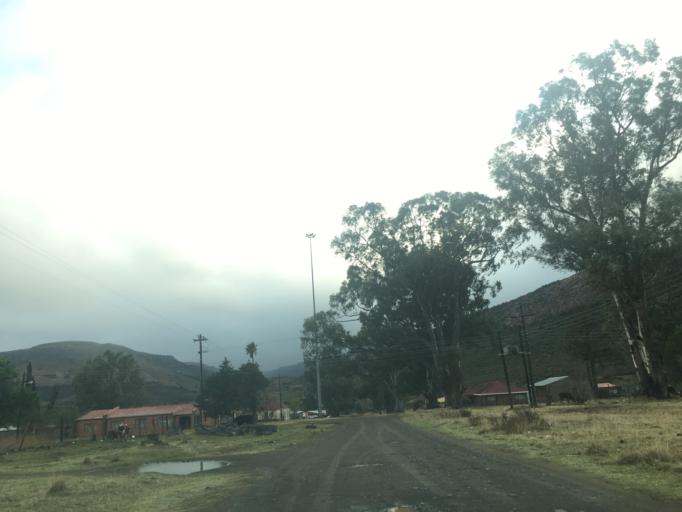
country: ZA
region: Eastern Cape
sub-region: Chris Hani District Municipality
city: Cala
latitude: -31.5227
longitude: 27.6997
